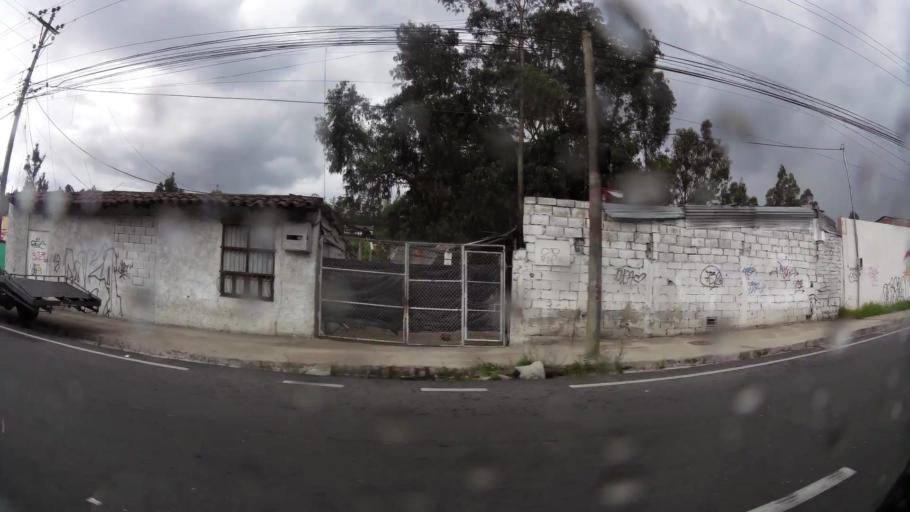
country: EC
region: Pichincha
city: Quito
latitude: -0.0923
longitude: -78.4879
